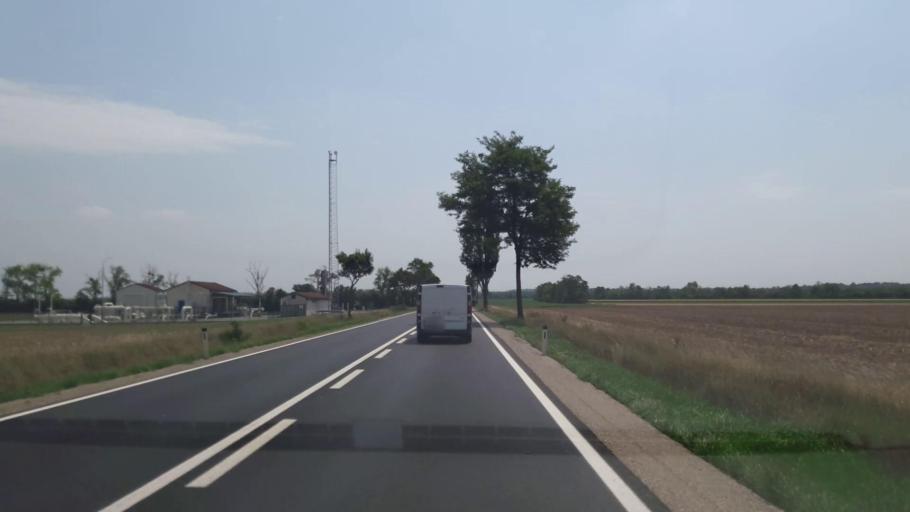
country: AT
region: Lower Austria
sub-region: Politischer Bezirk Wien-Umgebung
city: Rauchenwarth
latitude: 48.1240
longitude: 16.5077
